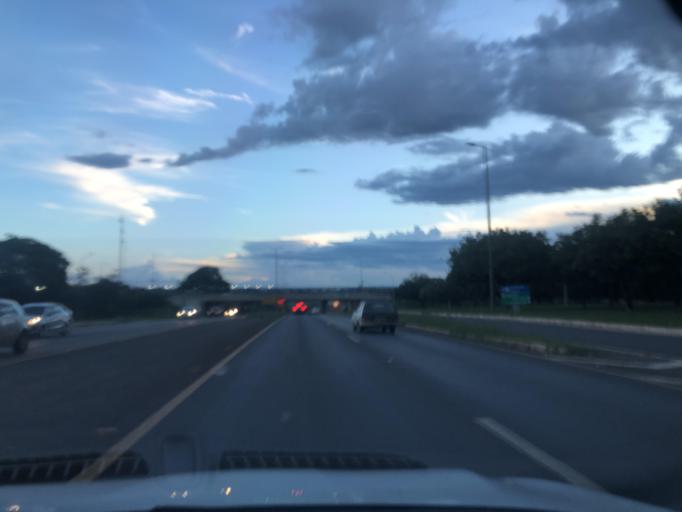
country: BR
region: Federal District
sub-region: Brasilia
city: Brasilia
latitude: -15.8427
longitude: -47.9327
